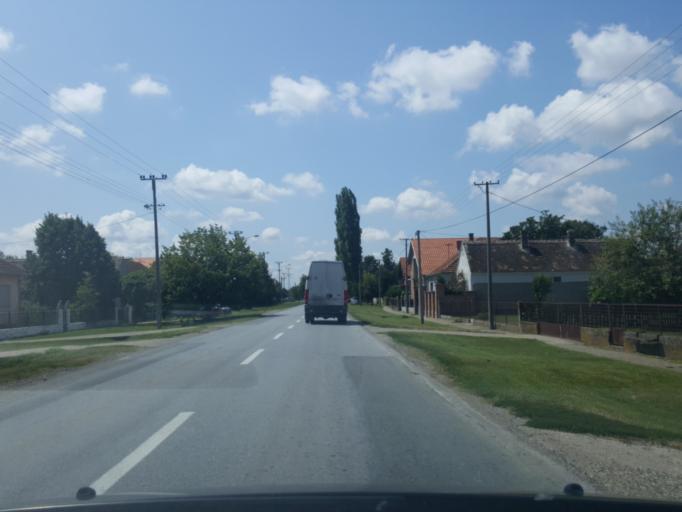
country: RS
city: Macvanska Mitrovica
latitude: 44.9553
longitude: 19.5984
